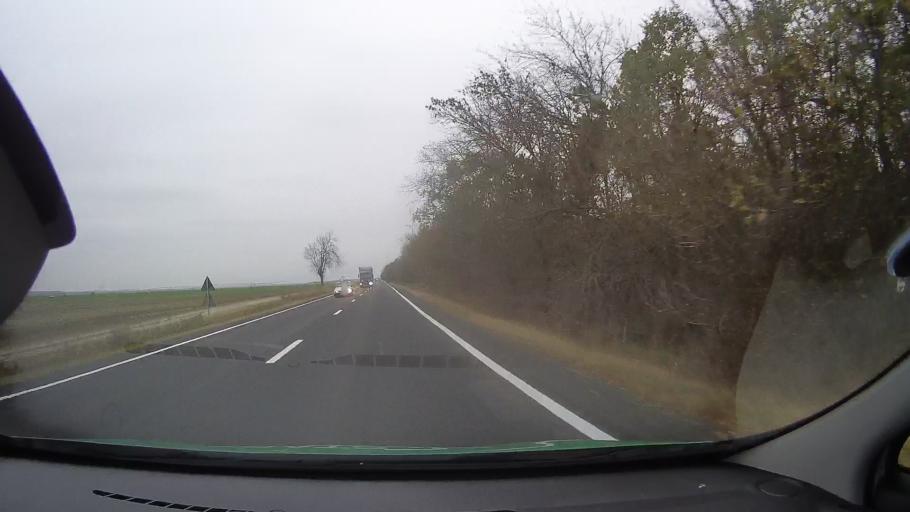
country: RO
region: Ialomita
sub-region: Comuna Mihail Kogalniceanu
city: Mihail Kogalniceanu
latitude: 44.6662
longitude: 27.7458
